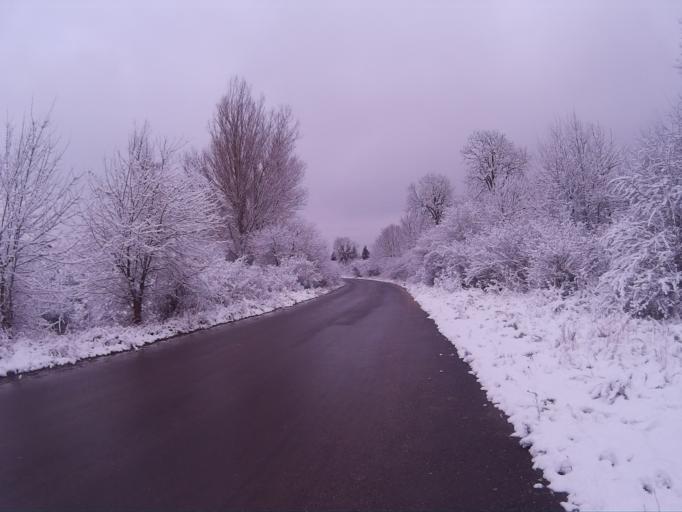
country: HU
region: Fejer
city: Szarliget
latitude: 47.5251
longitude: 18.5406
